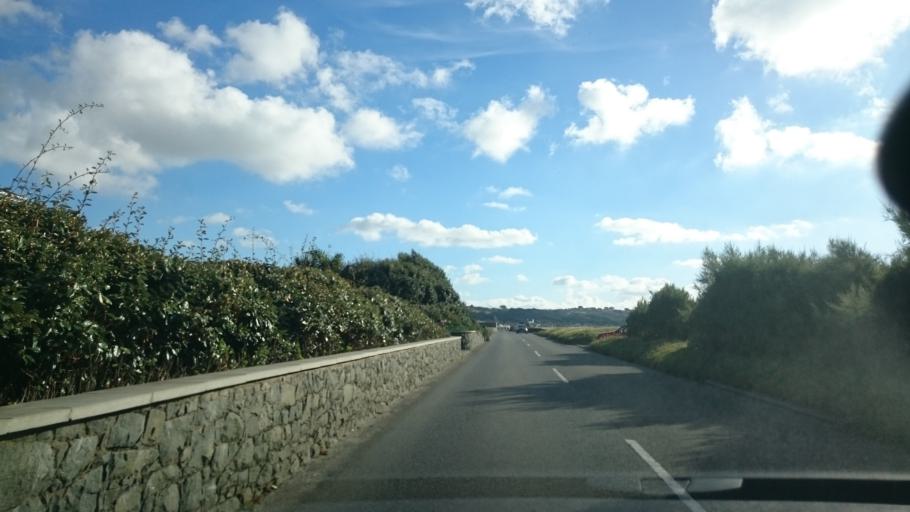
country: GG
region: St Peter Port
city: Saint Peter Port
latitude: 49.4525
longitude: -2.6501
